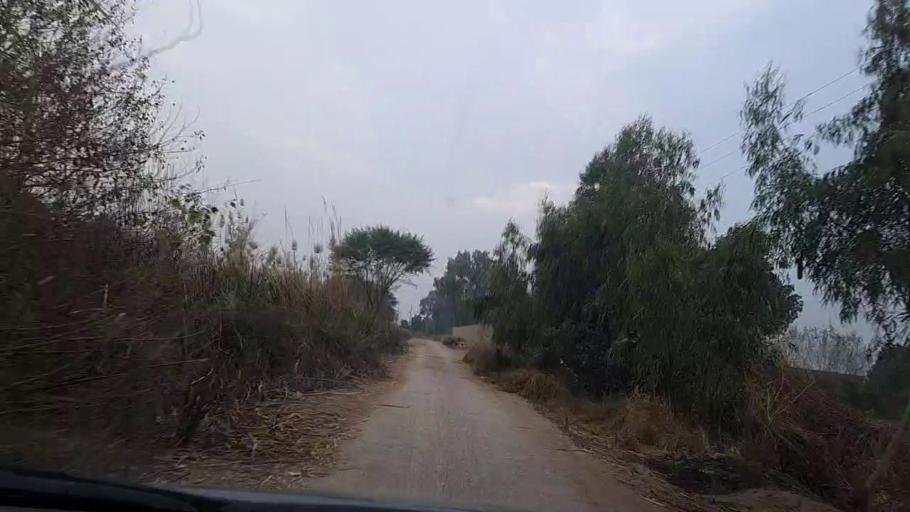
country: PK
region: Sindh
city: Sakrand
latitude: 26.2892
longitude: 68.2450
